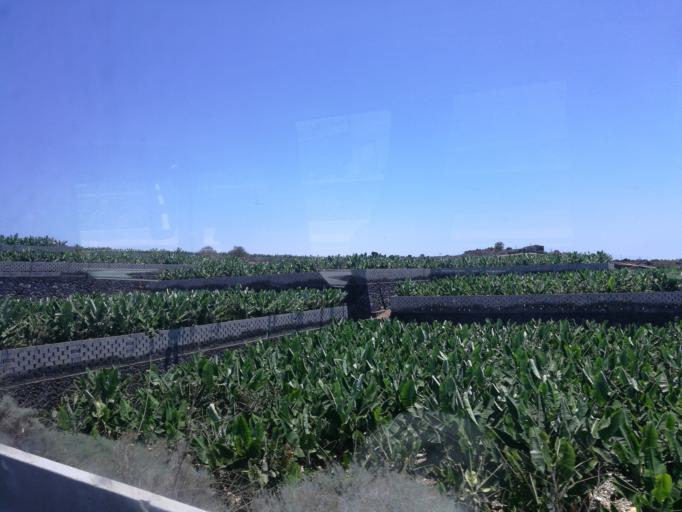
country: ES
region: Canary Islands
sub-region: Provincia de Santa Cruz de Tenerife
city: Guia de Isora
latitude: 28.1945
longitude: -16.8146
